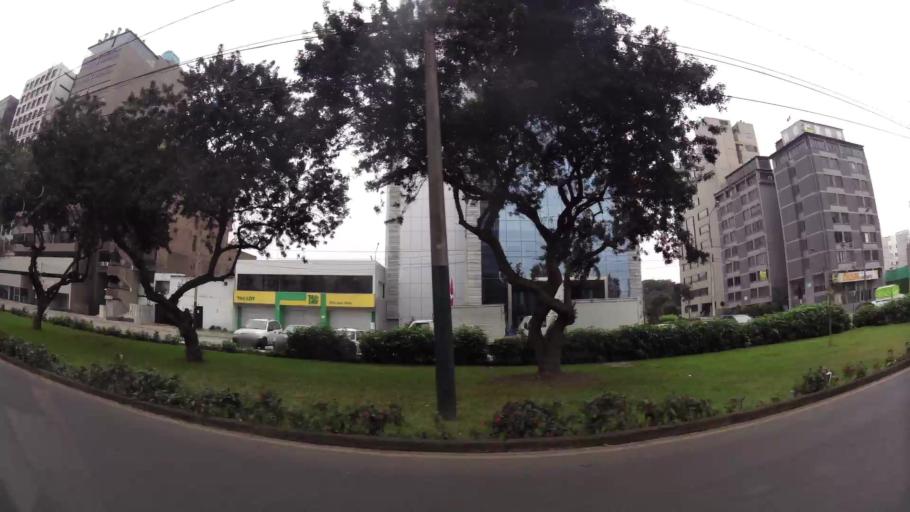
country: PE
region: Lima
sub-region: Lima
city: San Luis
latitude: -12.1000
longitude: -77.0195
